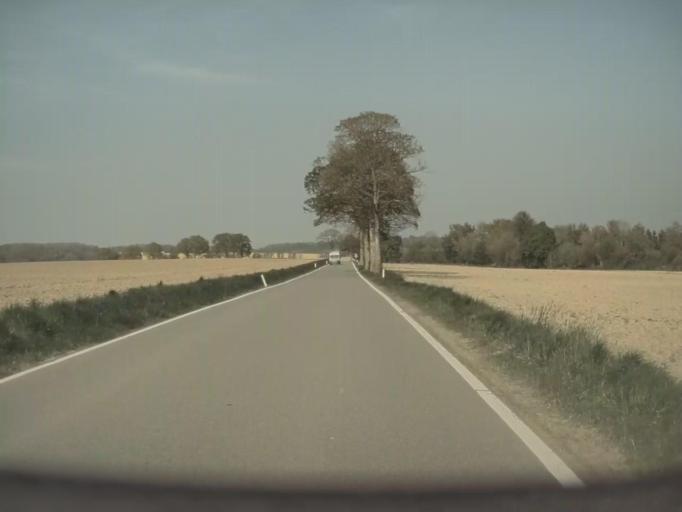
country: BE
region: Wallonia
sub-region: Province de Namur
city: Havelange
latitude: 50.3209
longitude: 5.2450
